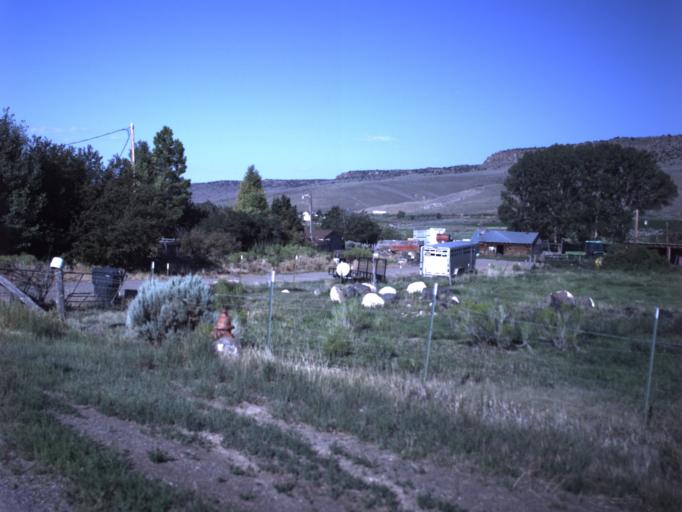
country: US
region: Utah
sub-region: Wayne County
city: Loa
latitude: 38.4684
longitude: -111.5936
